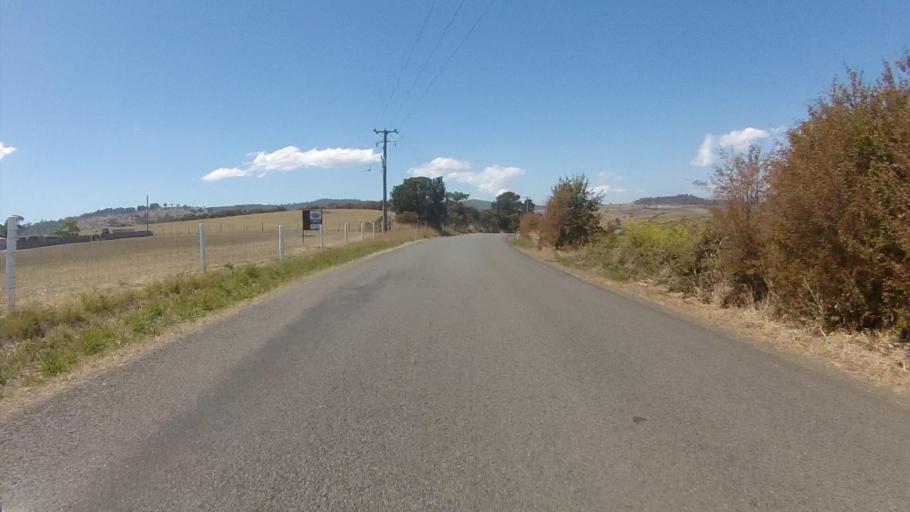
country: AU
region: Tasmania
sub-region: Sorell
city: Sorell
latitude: -42.7733
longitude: 147.5832
